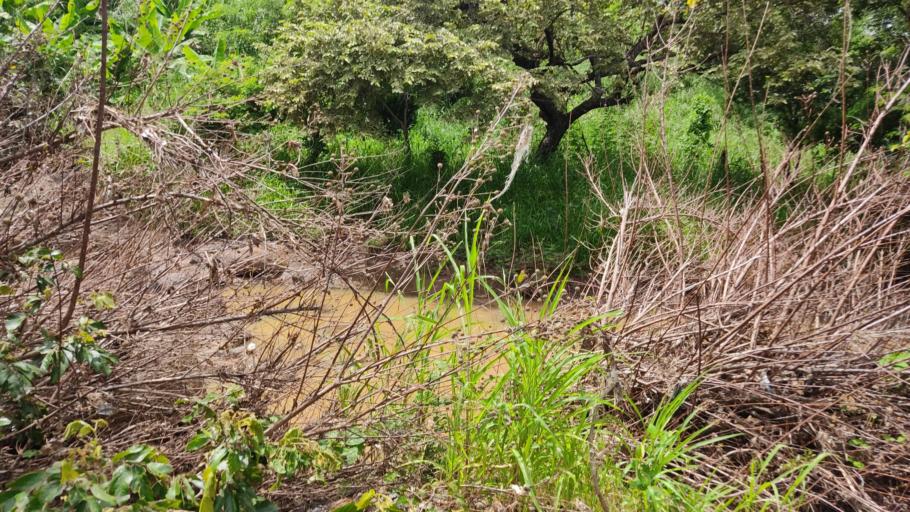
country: MX
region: Nayarit
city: Puga
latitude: 21.6663
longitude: -104.8519
